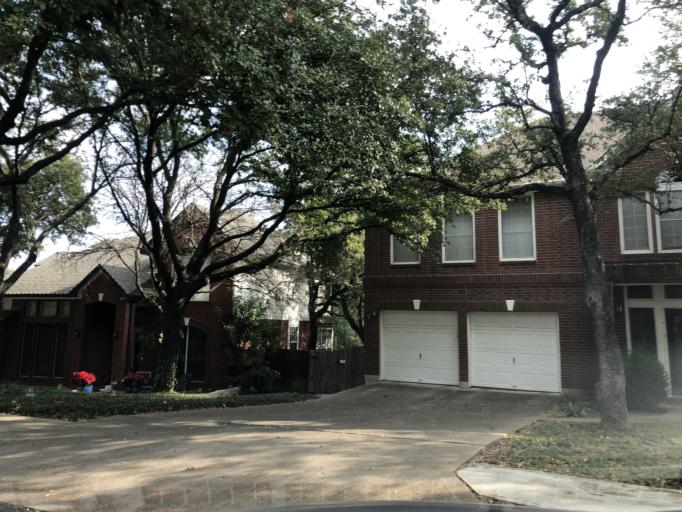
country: US
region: Texas
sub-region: Travis County
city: Wells Branch
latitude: 30.4169
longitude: -97.6817
